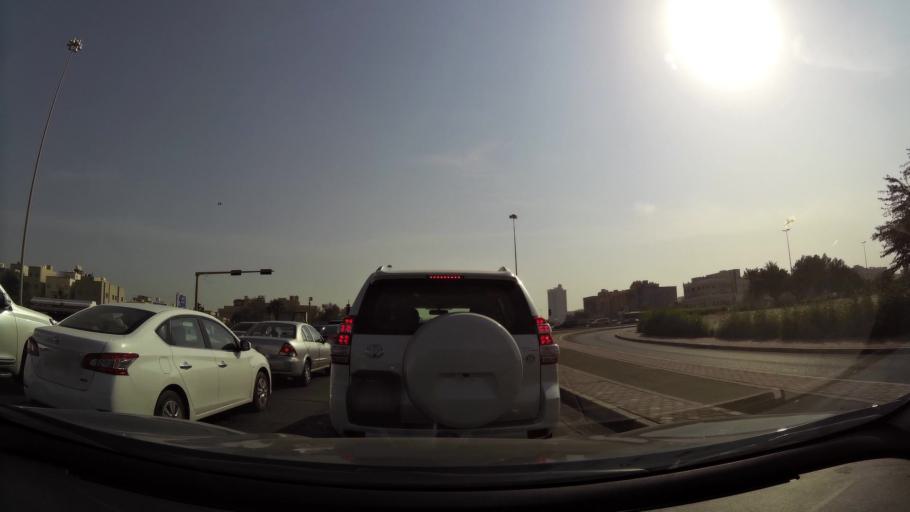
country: KW
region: Mubarak al Kabir
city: Mubarak al Kabir
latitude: 29.1818
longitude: 48.1019
